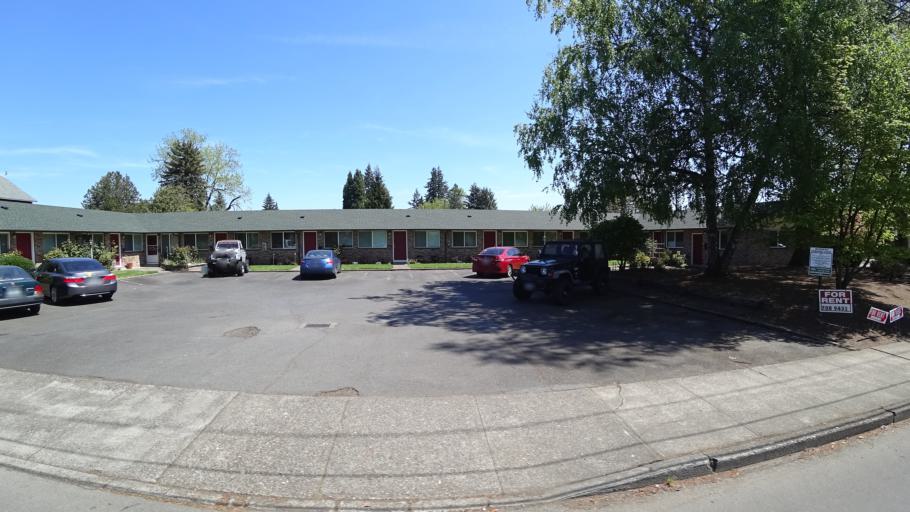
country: US
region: Oregon
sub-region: Washington County
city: Hillsboro
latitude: 45.5178
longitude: -122.9702
